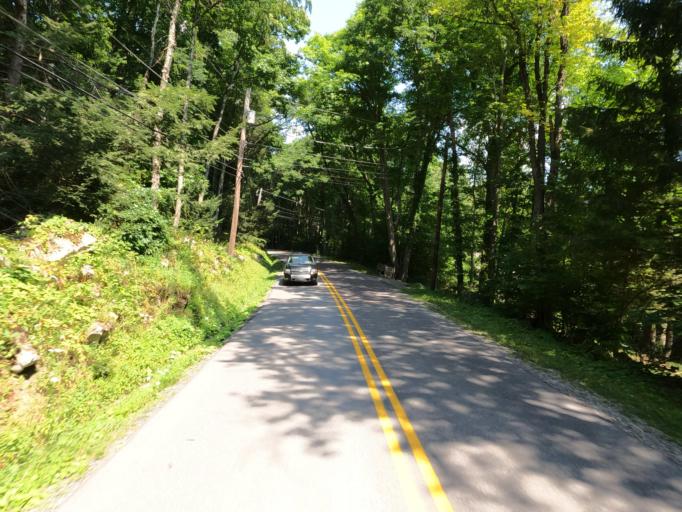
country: US
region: Maryland
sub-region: Garrett County
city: Oakland
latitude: 39.4983
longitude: -79.3718
